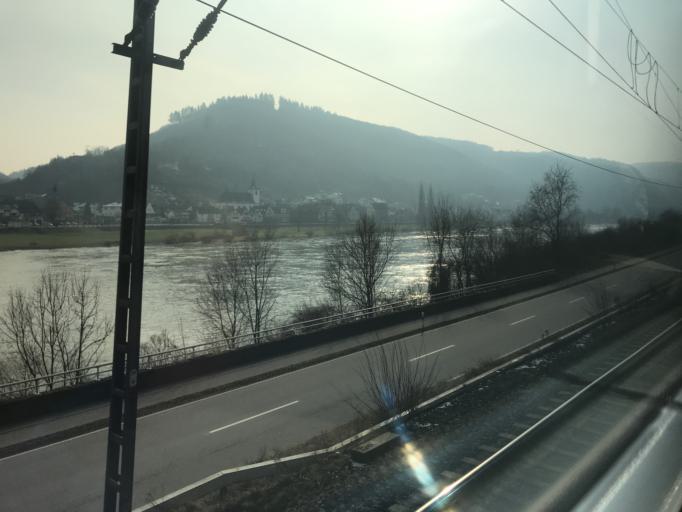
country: DE
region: Rheinland-Pfalz
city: Burgen
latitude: 50.2151
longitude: 7.3853
